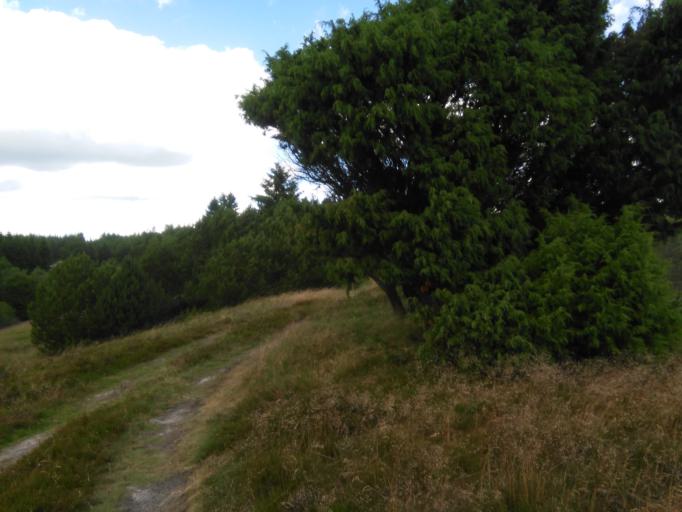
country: DK
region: Central Jutland
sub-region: Silkeborg Kommune
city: Virklund
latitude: 56.0636
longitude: 9.4468
